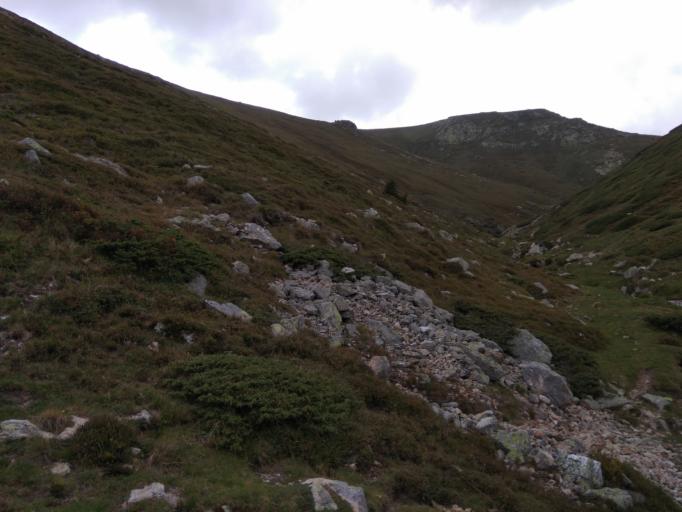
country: BG
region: Plovdiv
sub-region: Obshtina Karlovo
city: Karlovo
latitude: 42.7076
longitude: 24.8808
